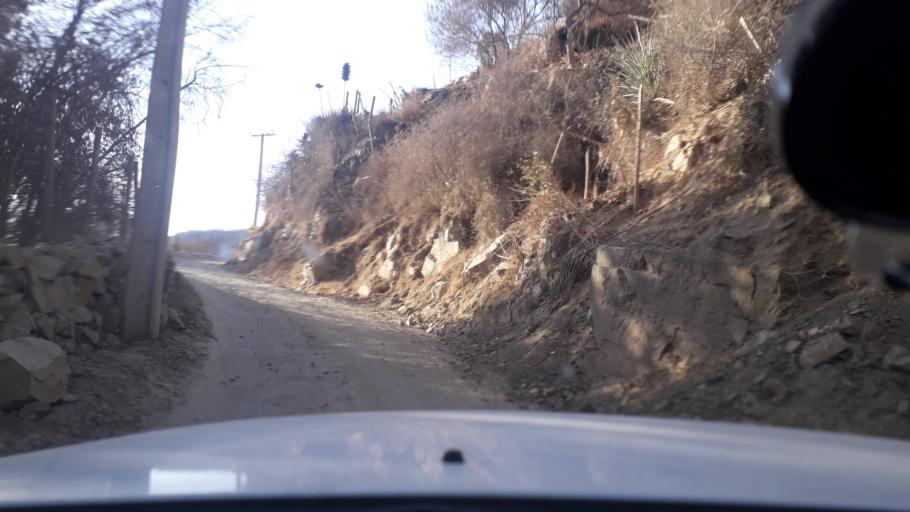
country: CL
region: Valparaiso
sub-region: Provincia de Marga Marga
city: Limache
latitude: -33.0537
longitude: -71.0890
